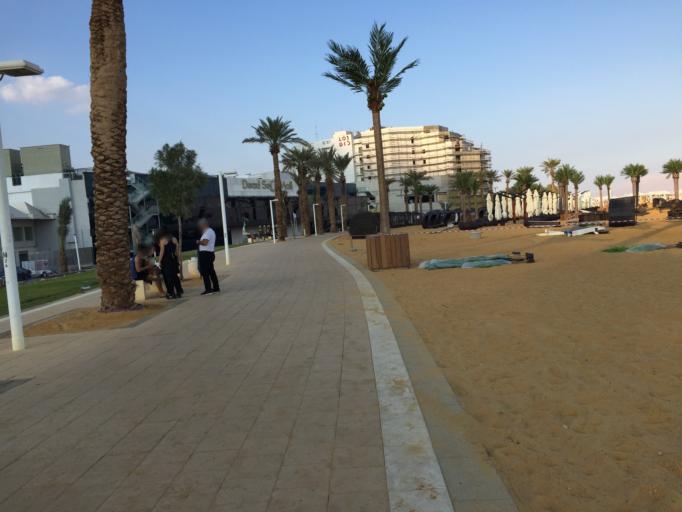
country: IL
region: Southern District
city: `En Boqeq
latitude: 31.1976
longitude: 35.3641
